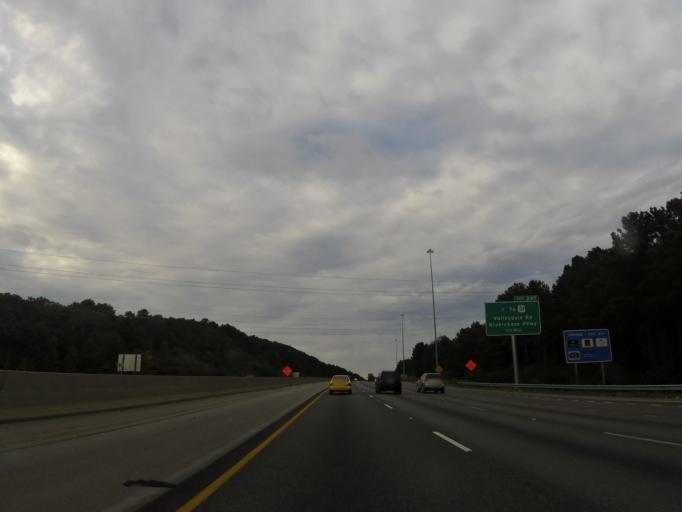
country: US
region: Alabama
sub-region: Shelby County
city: Indian Springs Village
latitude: 33.3444
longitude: -86.7804
